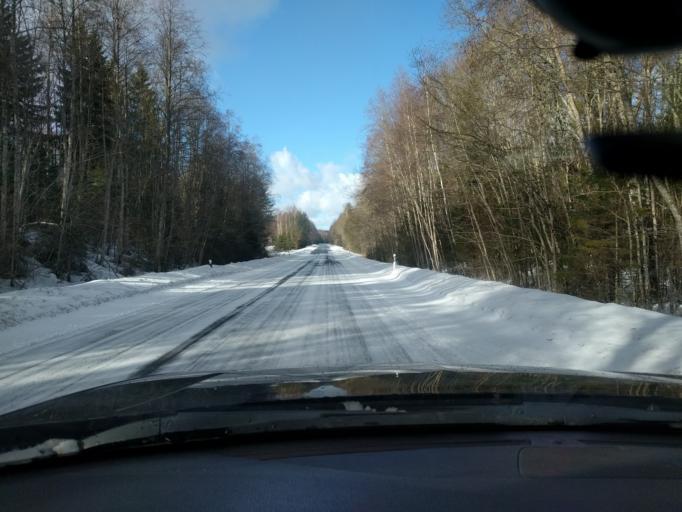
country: EE
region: Harju
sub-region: Anija vald
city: Kehra
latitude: 59.2126
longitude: 25.5029
